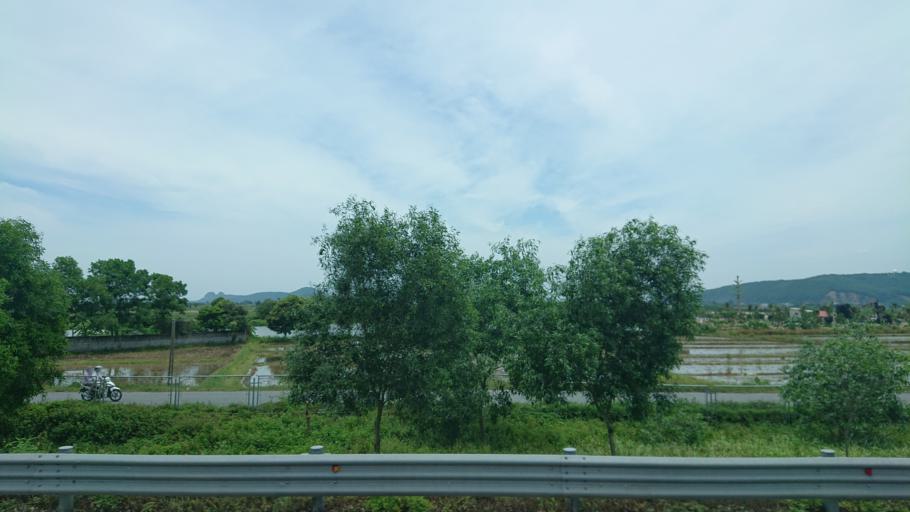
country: VN
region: Hai Phong
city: Tien Lang
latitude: 20.7709
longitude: 106.5965
